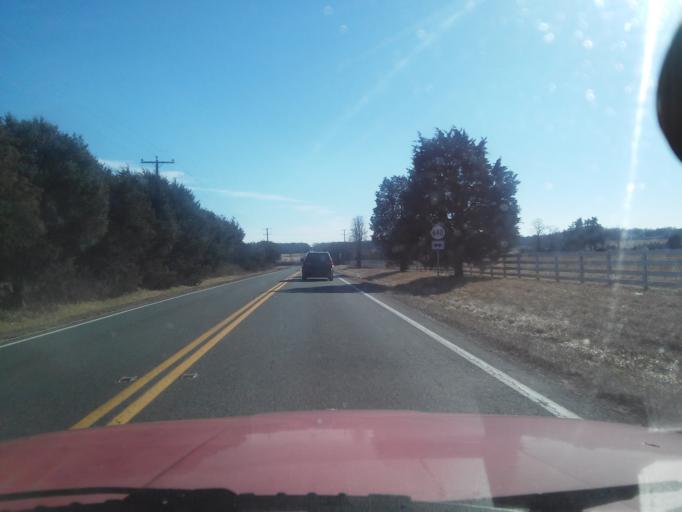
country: US
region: Virginia
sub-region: Orange County
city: Gordonsville
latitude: 38.0265
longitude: -78.1905
